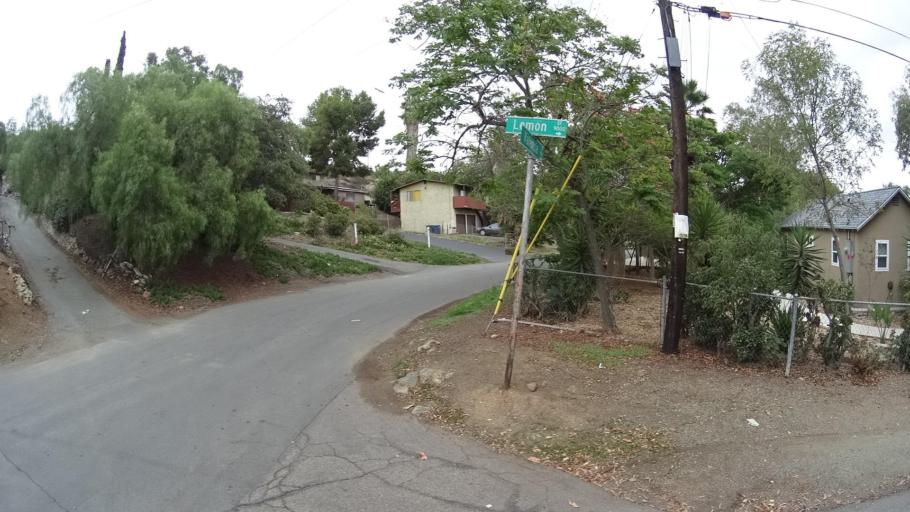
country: US
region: California
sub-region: San Diego County
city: Spring Valley
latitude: 32.7329
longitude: -117.0033
